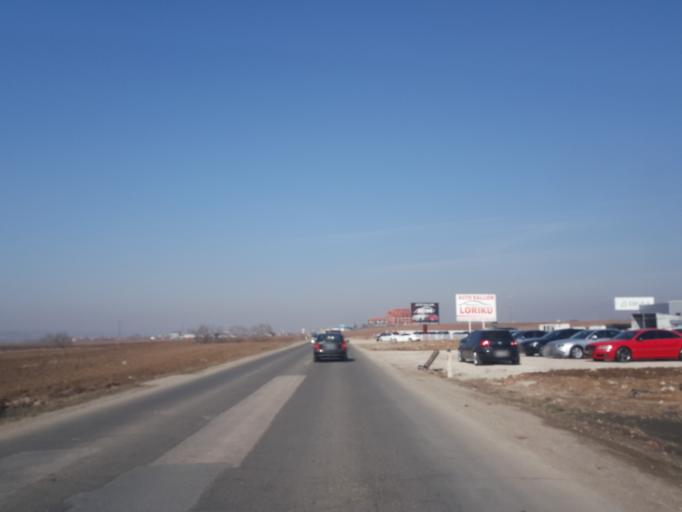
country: XK
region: Mitrovica
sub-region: Vushtrri
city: Vushtrri
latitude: 42.7699
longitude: 21.0215
